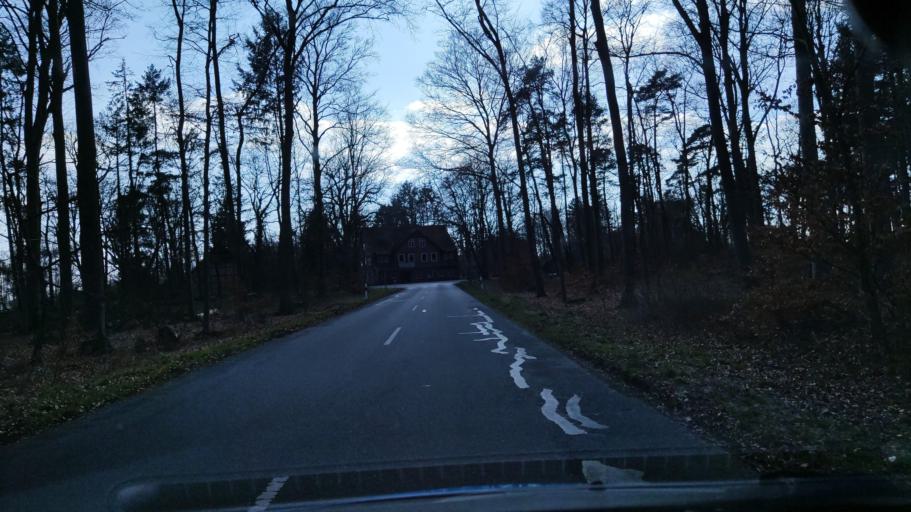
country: DE
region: Lower Saxony
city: Damnatz
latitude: 53.1037
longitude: 11.1523
